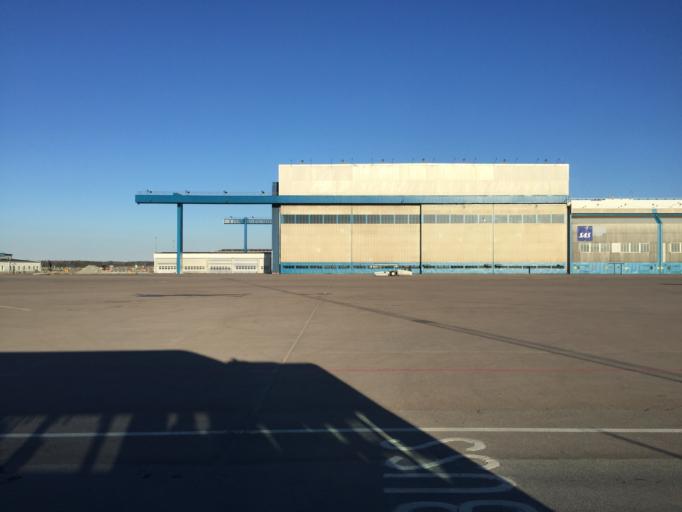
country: SE
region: Stockholm
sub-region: Sigtuna Kommun
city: Rosersberg
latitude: 59.6544
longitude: 17.9422
